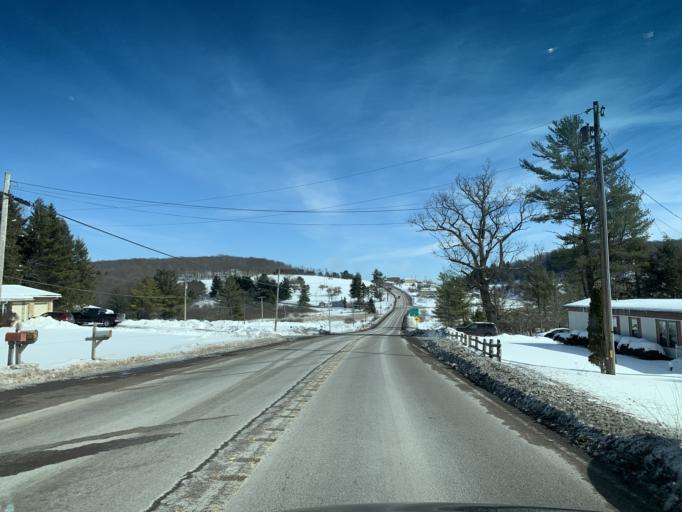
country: US
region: Pennsylvania
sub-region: Somerset County
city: Meyersdale
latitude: 39.6857
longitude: -79.0773
